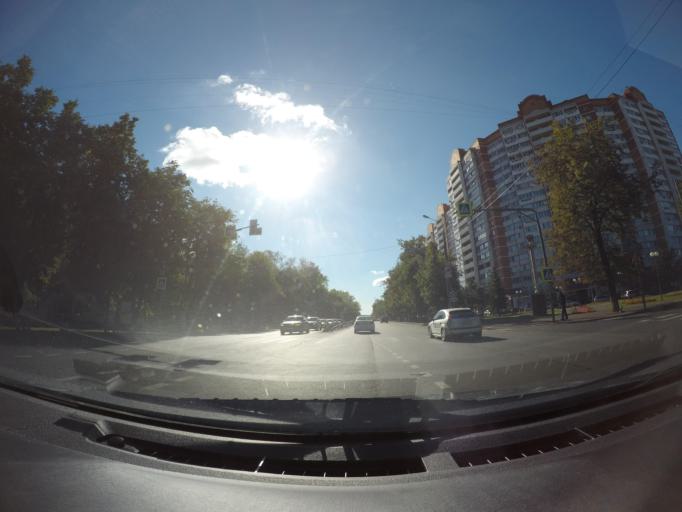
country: RU
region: Moscow
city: Zhulebino
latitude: 55.6937
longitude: 37.8644
